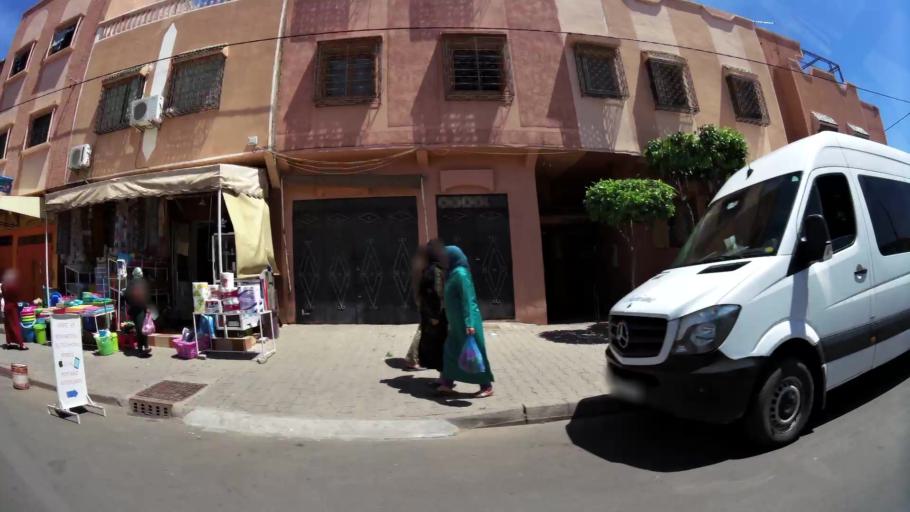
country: MA
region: Marrakech-Tensift-Al Haouz
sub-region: Marrakech
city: Marrakesh
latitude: 31.6393
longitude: -8.0526
